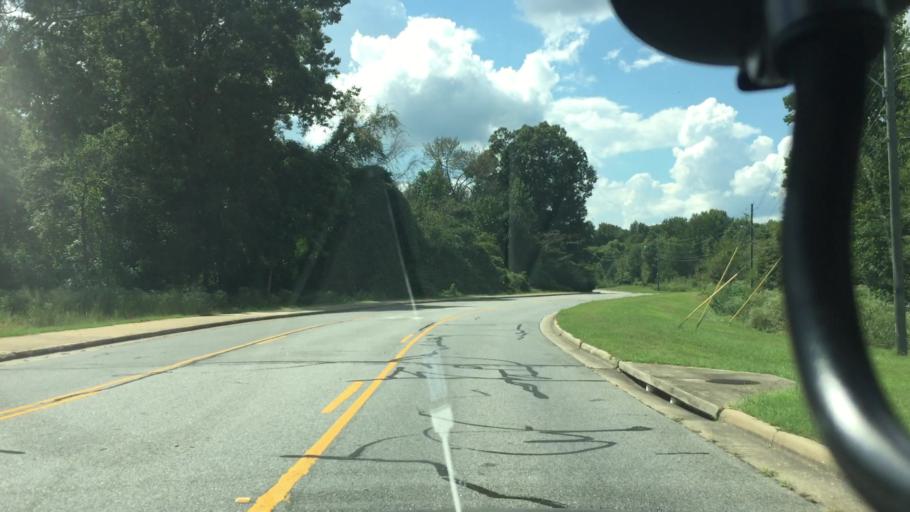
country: US
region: Alabama
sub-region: Lee County
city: Auburn
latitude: 32.5727
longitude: -85.5070
